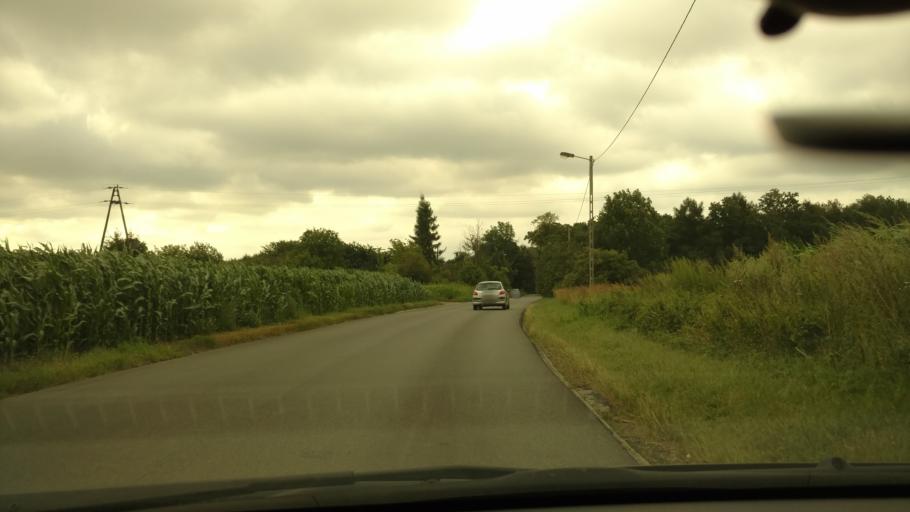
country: PL
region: Lesser Poland Voivodeship
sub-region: Powiat krakowski
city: Zielonki
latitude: 50.1130
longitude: 19.9431
